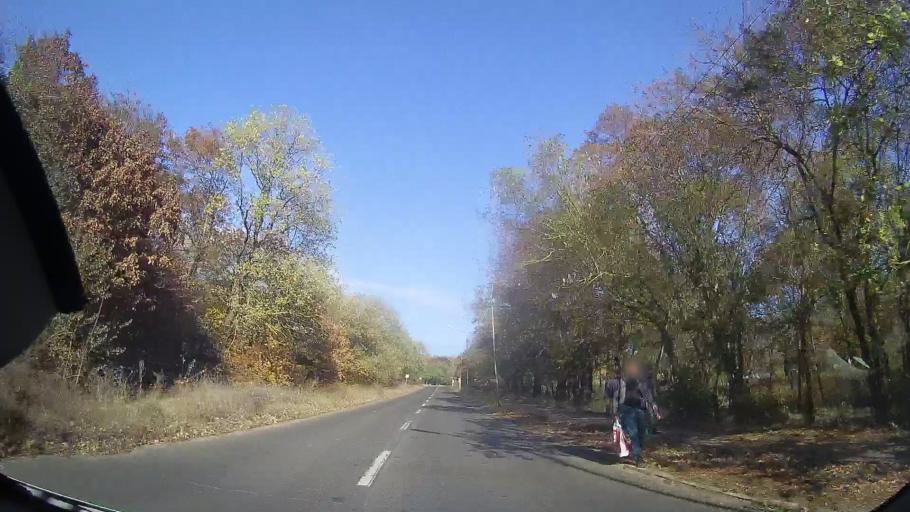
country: RO
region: Constanta
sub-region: Comuna Douazeci si Trei August
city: Douazeci si Trei August
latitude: 43.8734
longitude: 28.5968
